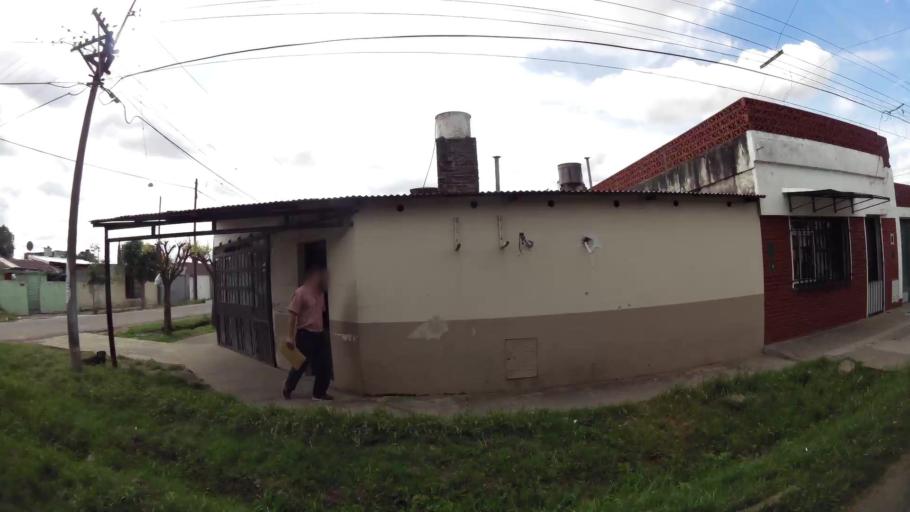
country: AR
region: Santa Fe
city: Gobernador Galvez
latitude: -33.0140
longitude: -60.6464
